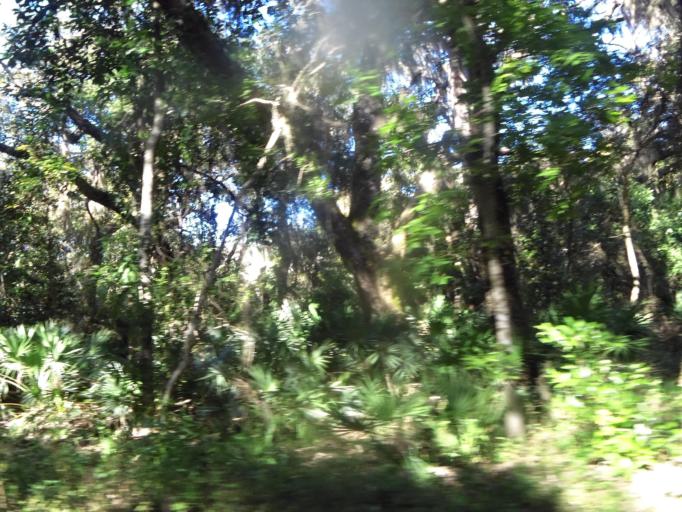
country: US
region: Florida
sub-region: Duval County
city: Atlantic Beach
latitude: 30.4353
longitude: -81.4317
